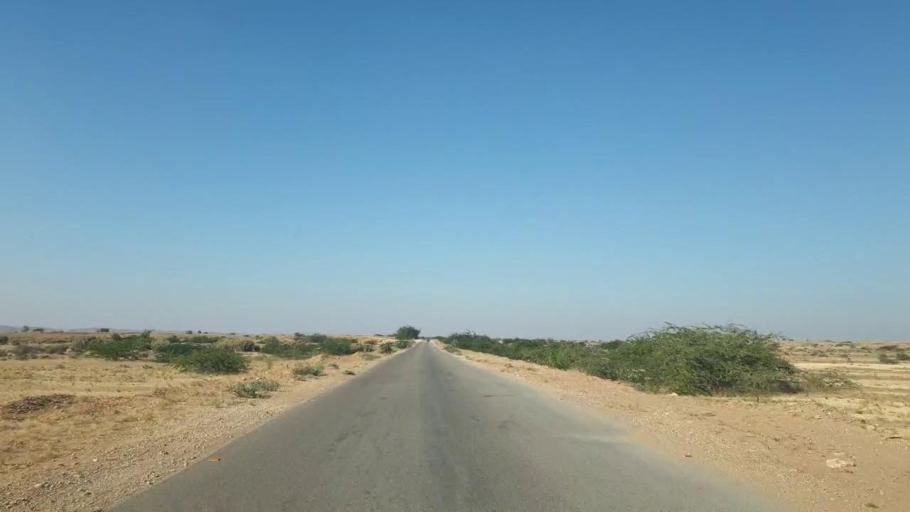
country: PK
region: Sindh
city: Malir Cantonment
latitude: 25.2547
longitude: 67.6022
